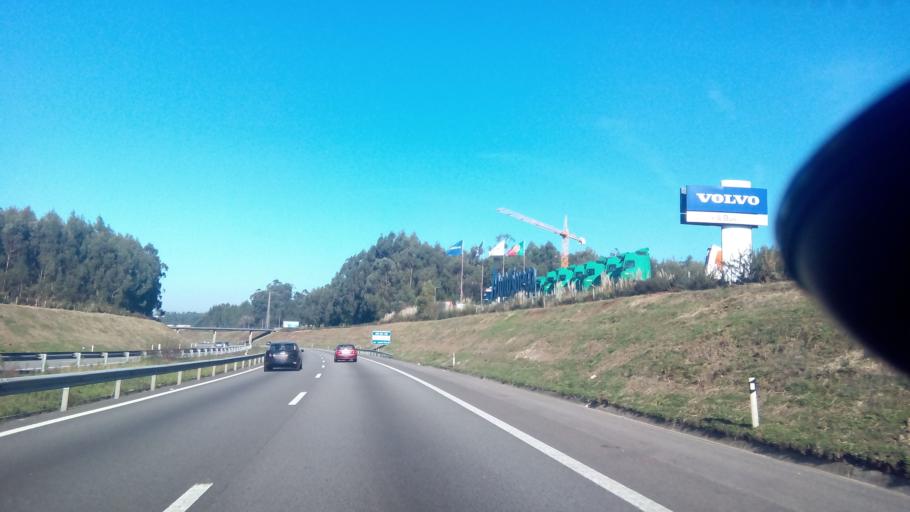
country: PT
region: Porto
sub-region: Matosinhos
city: Santa Cruz do Bispo
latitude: 41.2434
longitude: -8.6942
